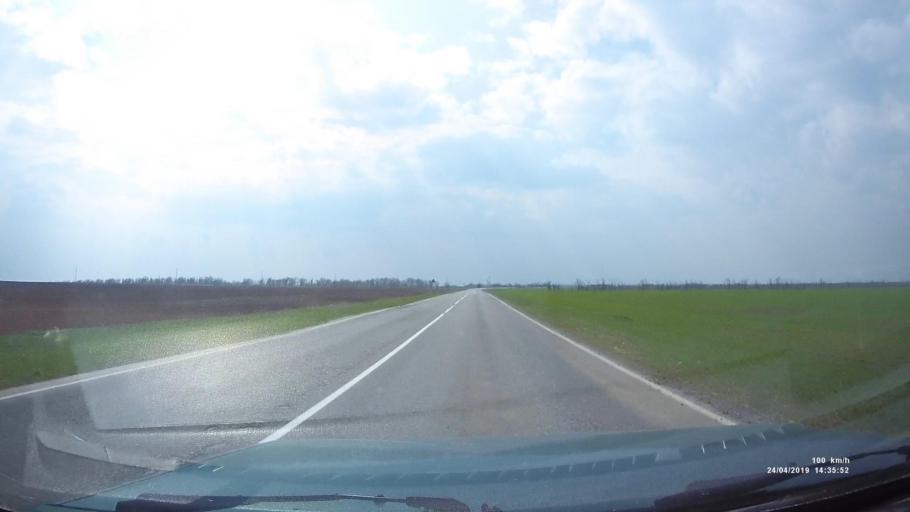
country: RU
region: Rostov
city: Remontnoye
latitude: 46.3740
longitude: 43.9015
